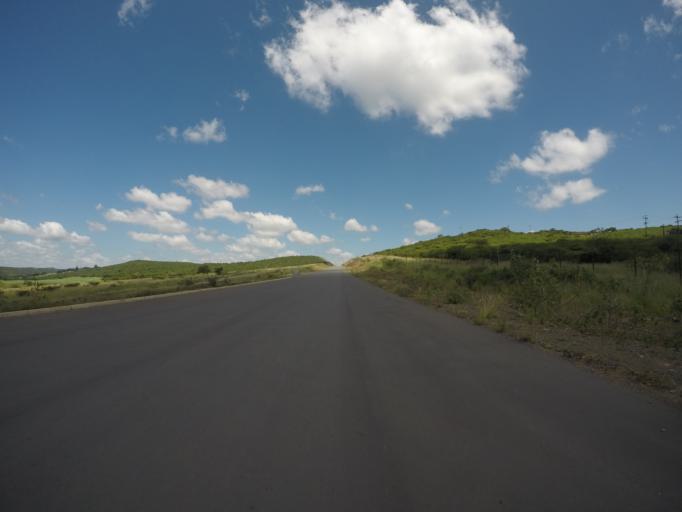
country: ZA
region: KwaZulu-Natal
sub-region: uThungulu District Municipality
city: Empangeni
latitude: -28.6199
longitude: 31.7563
